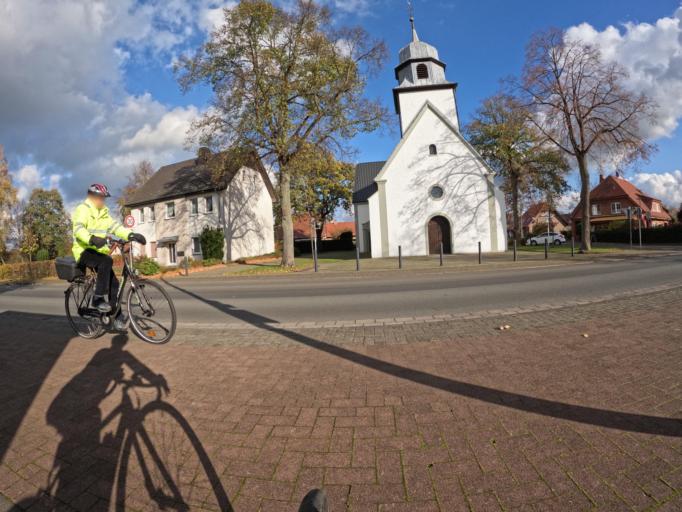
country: DE
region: North Rhine-Westphalia
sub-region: Regierungsbezirk Detmold
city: Hovelhof
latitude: 51.8211
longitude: 8.5930
